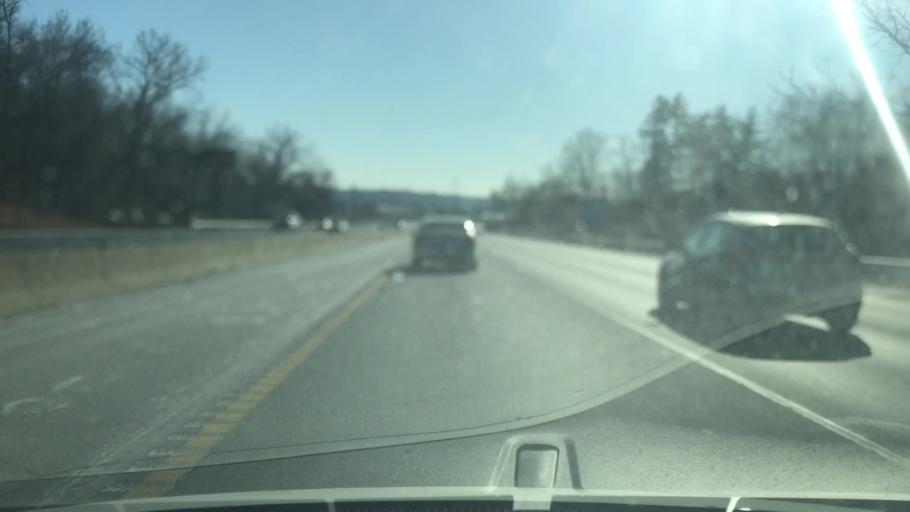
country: US
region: Missouri
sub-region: Clay County
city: North Kansas City
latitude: 39.1516
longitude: -94.5598
